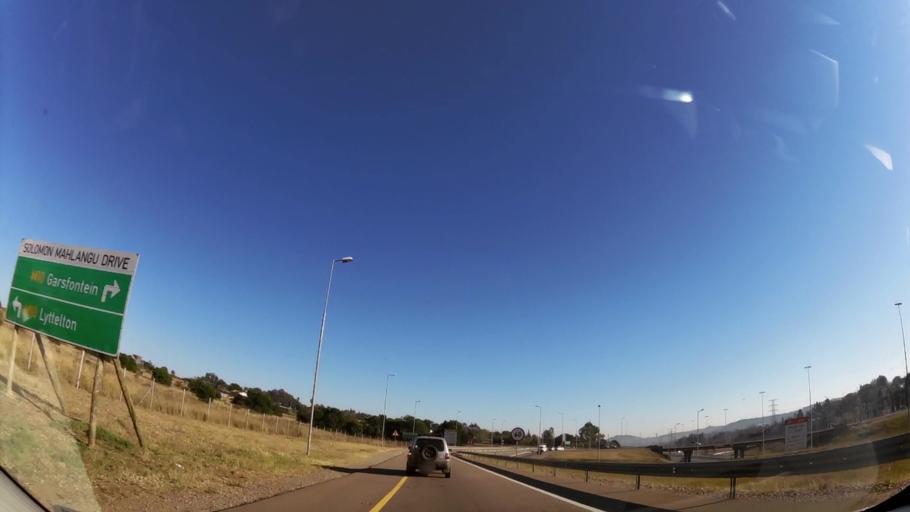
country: ZA
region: Gauteng
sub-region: City of Tshwane Metropolitan Municipality
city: Centurion
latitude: -25.8157
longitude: 28.2349
